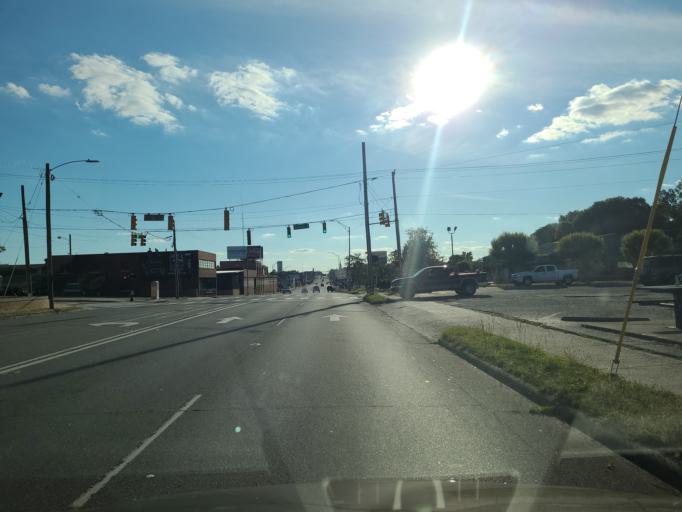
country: US
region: North Carolina
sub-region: Gaston County
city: Gastonia
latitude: 35.2625
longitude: -81.1678
